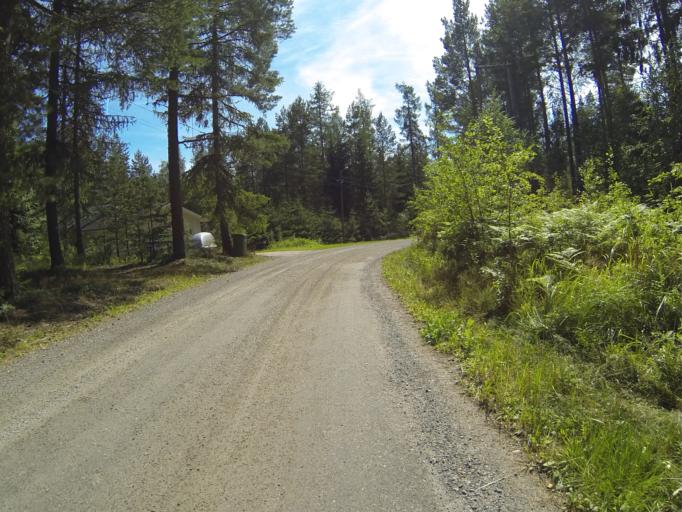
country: FI
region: Varsinais-Suomi
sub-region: Salo
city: Saerkisalo
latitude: 60.2617
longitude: 22.9738
